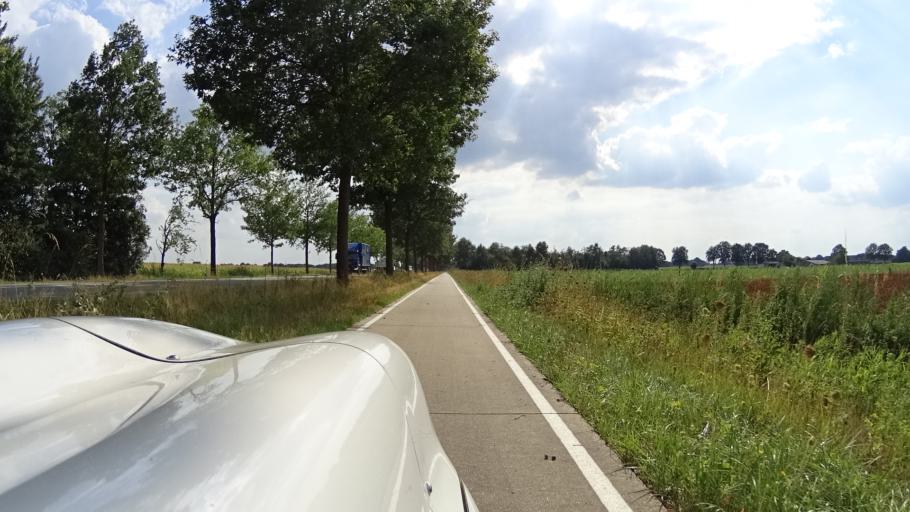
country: NL
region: North Brabant
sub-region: Gemeente Sint Anthonis
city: Sint Anthonis
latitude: 51.6183
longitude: 5.8748
